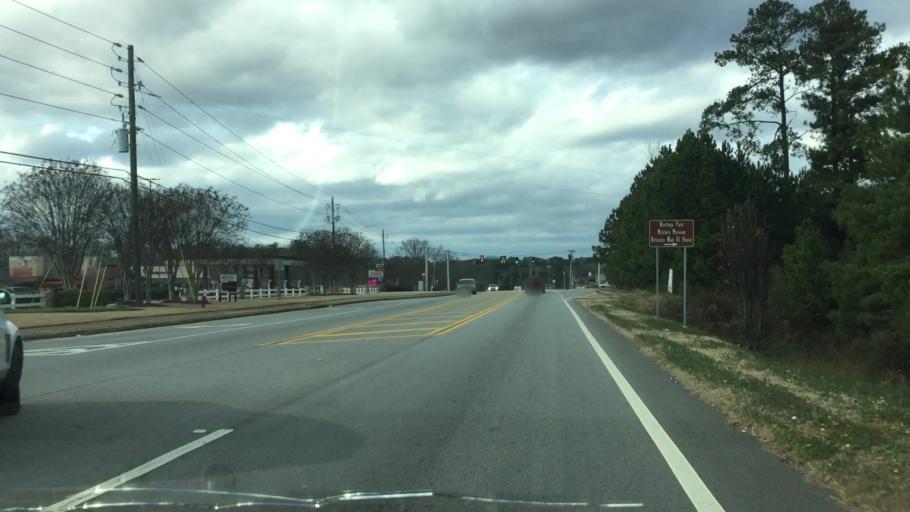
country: US
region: Georgia
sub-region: Henry County
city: McDonough
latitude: 33.4382
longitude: -84.1200
